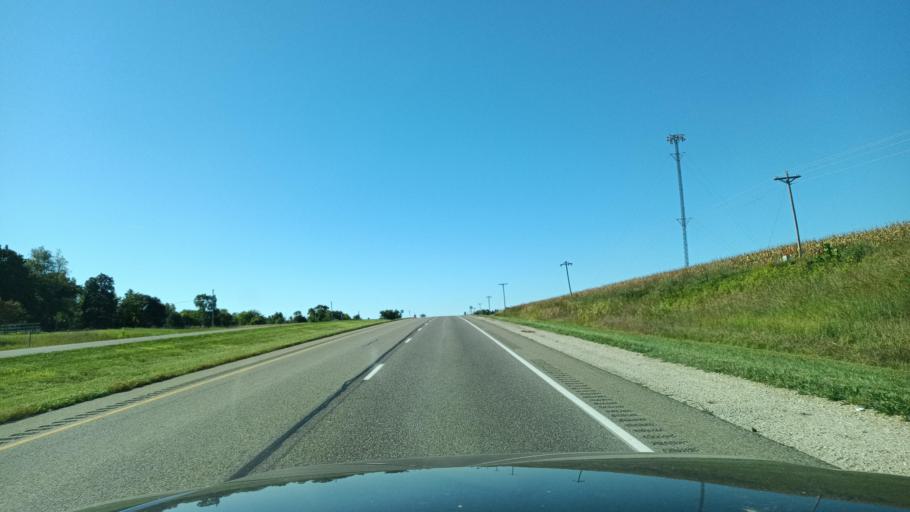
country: US
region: Iowa
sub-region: Lee County
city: Fort Madison
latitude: 40.6893
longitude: -91.2497
